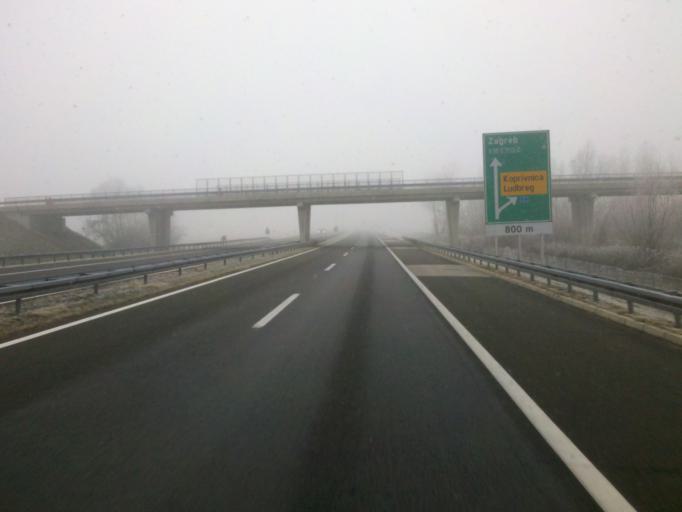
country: HR
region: Medimurska
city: Orehovica
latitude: 46.2954
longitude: 16.4949
